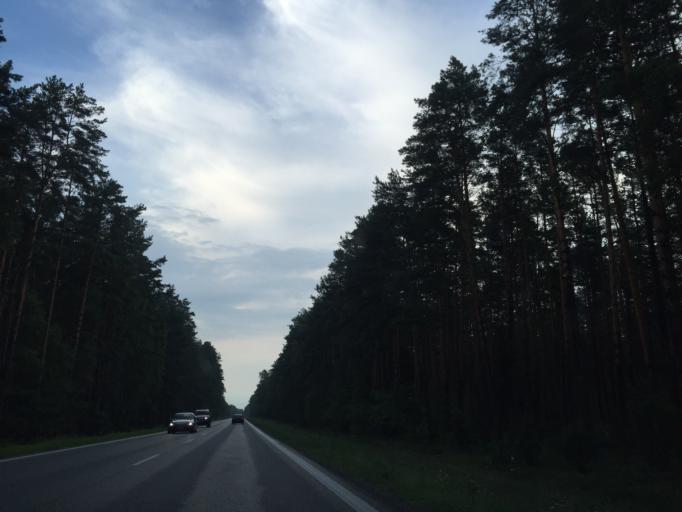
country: PL
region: Masovian Voivodeship
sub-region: Powiat ostrowski
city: Brok
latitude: 52.7306
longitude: 21.8513
